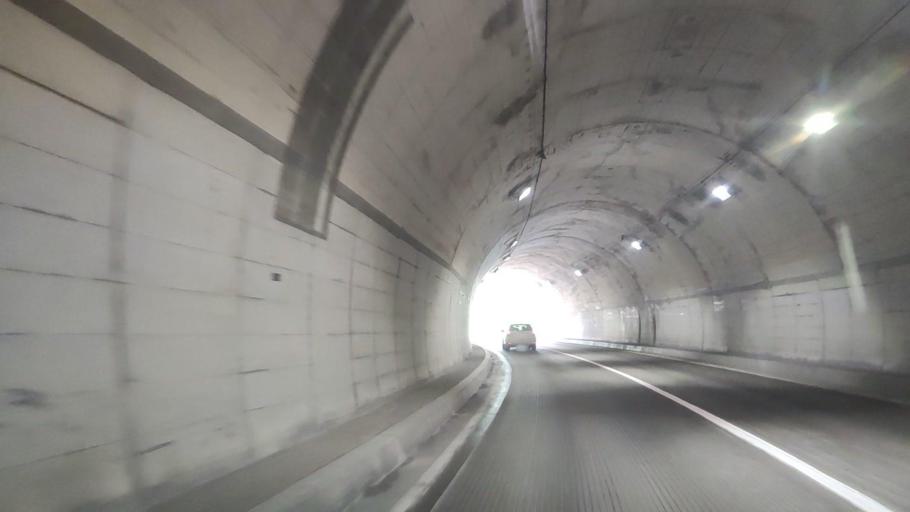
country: JP
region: Hokkaido
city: Ishikari
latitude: 43.4811
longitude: 141.3900
